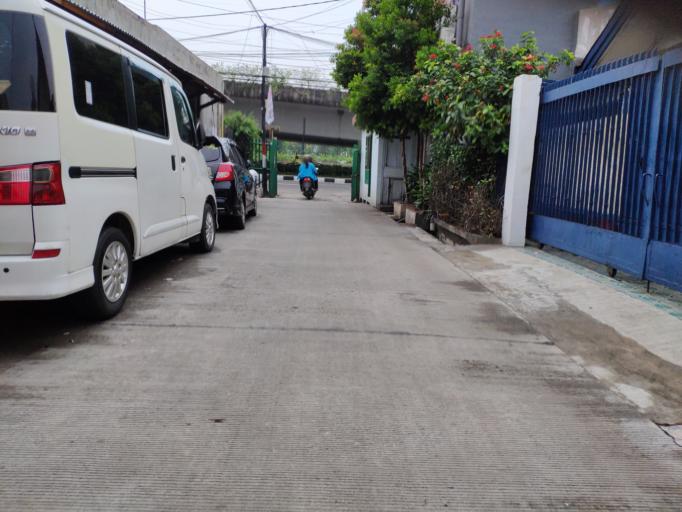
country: ID
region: Jakarta Raya
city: Jakarta
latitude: -6.1990
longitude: 106.8550
